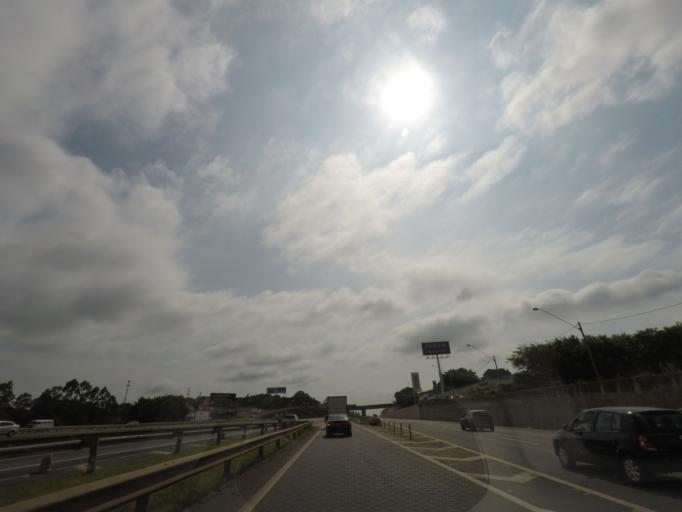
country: BR
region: Sao Paulo
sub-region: Campinas
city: Campinas
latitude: -22.8426
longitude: -47.0573
